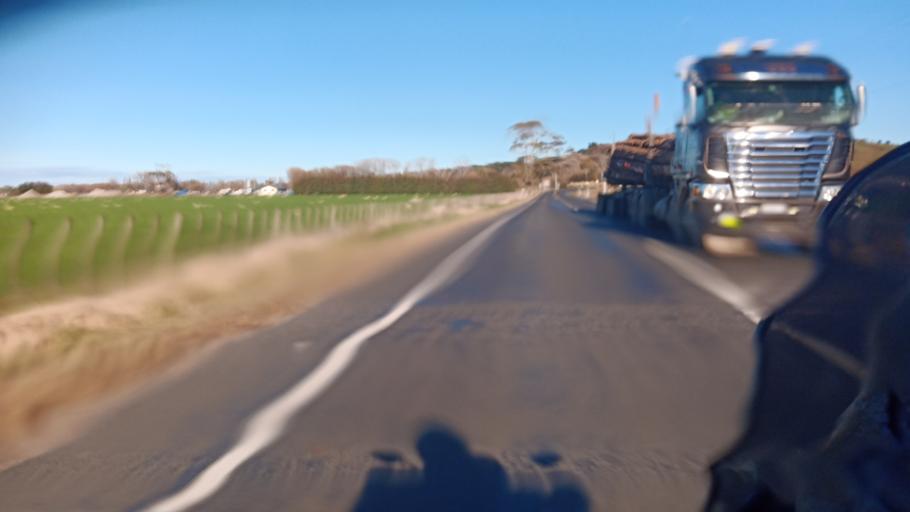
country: NZ
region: Hawke's Bay
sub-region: Napier City
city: Napier
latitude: -39.3907
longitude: 176.8824
